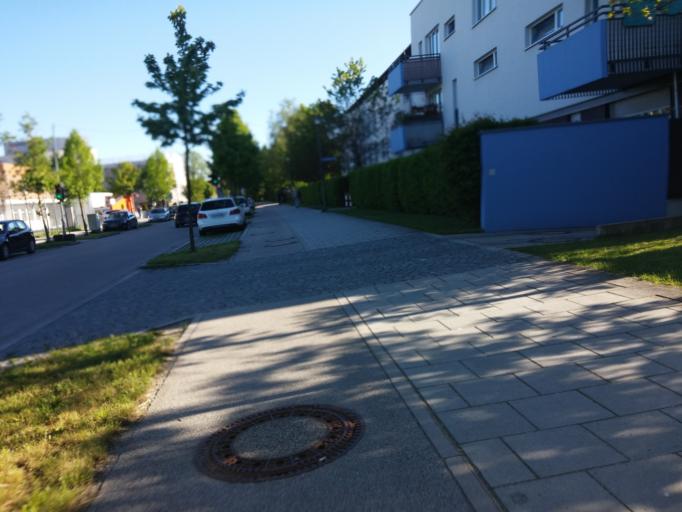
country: DE
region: Bavaria
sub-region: Upper Bavaria
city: Haar
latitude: 48.1131
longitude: 11.7152
